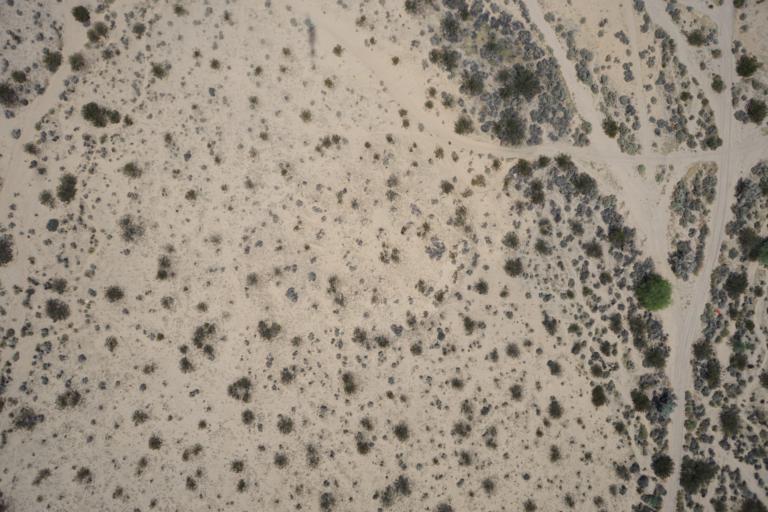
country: US
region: California
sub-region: San Bernardino County
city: Twentynine Palms
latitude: 34.1592
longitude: -116.0463
